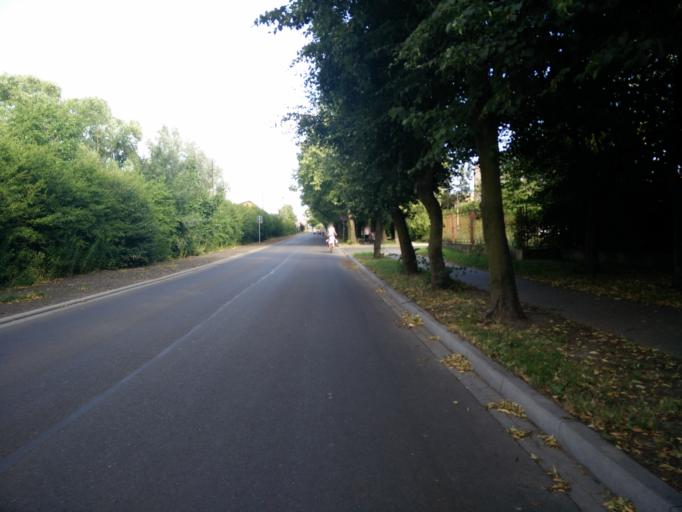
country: PL
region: Greater Poland Voivodeship
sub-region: Powiat sredzki
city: Sroda Wielkopolska
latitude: 52.2337
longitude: 17.2615
